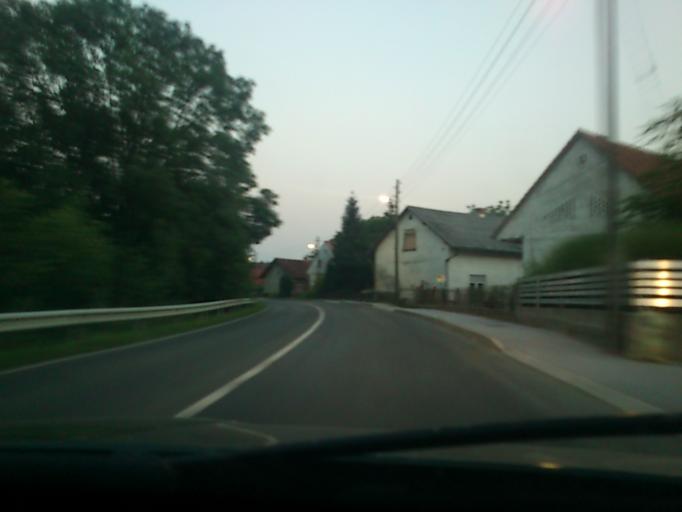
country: SI
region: Duplek
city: Spodnji Duplek
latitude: 46.4873
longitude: 15.7309
